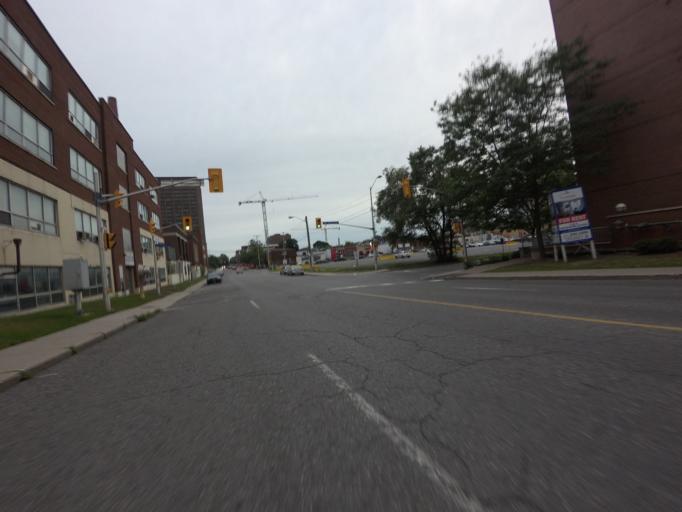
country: CA
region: Ontario
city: Ottawa
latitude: 45.4021
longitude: -75.7078
